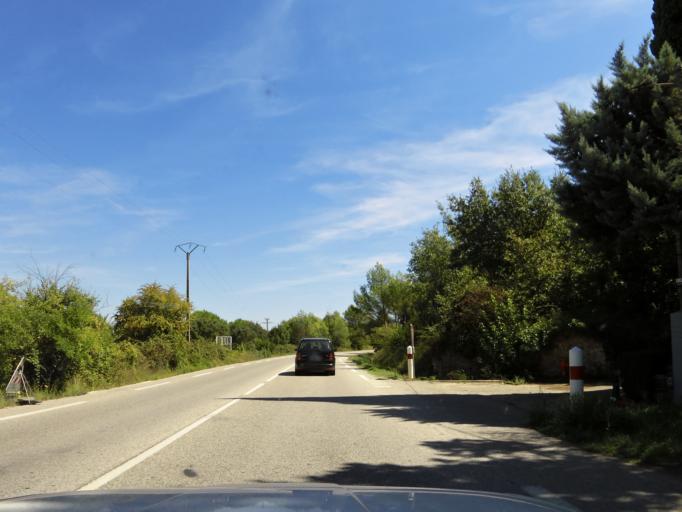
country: FR
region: Languedoc-Roussillon
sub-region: Departement du Gard
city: Bagnols-sur-Ceze
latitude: 44.1681
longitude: 4.5989
